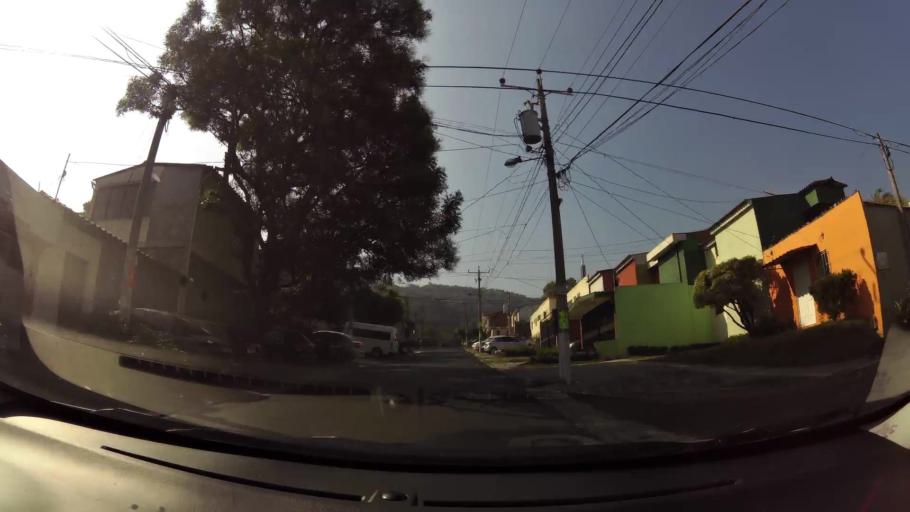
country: SV
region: La Libertad
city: Antiguo Cuscatlan
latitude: 13.6700
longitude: -89.2269
